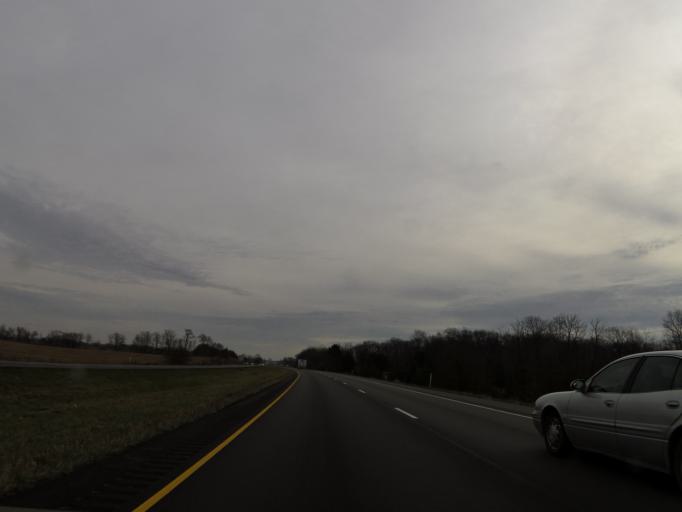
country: US
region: Indiana
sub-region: Montgomery County
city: Crawfordsville
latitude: 40.0995
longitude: -87.0483
